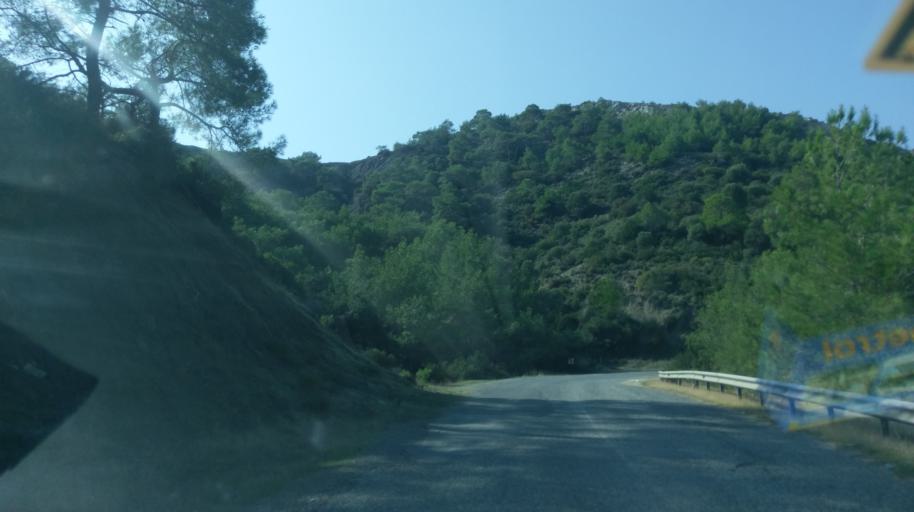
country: CY
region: Keryneia
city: Lapithos
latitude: 35.3519
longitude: 33.0731
